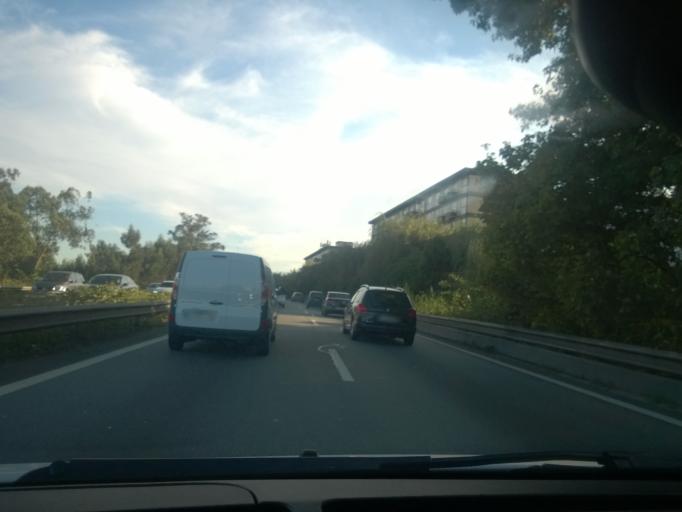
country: PT
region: Porto
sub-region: Matosinhos
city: Senhora da Hora
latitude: 41.1932
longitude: -8.6285
